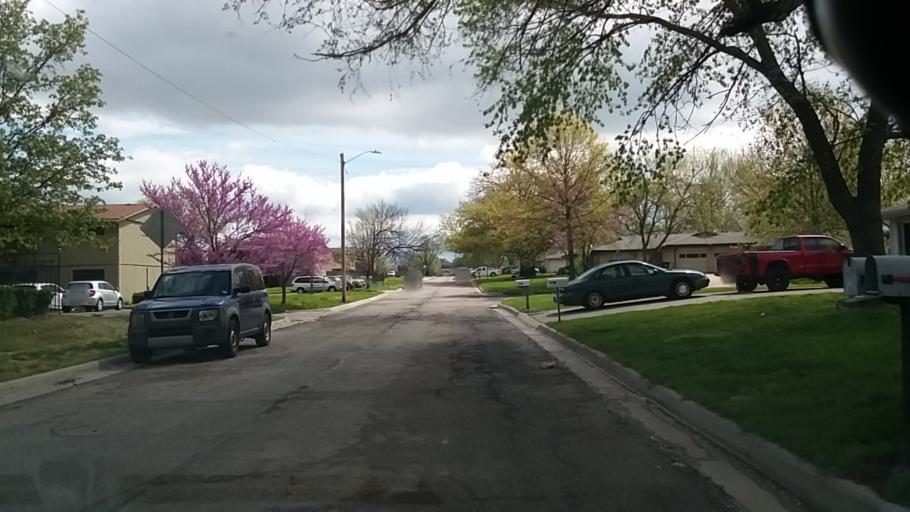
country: US
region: Kansas
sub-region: Douglas County
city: Lawrence
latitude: 38.9412
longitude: -95.2487
